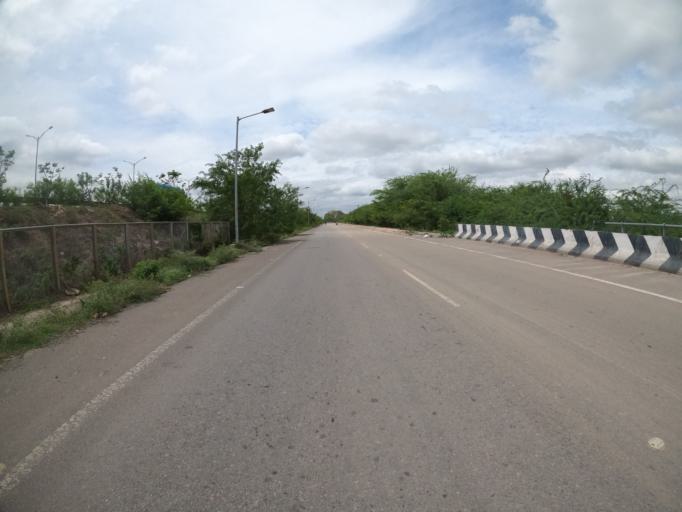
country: IN
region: Telangana
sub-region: Hyderabad
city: Hyderabad
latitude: 17.3026
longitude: 78.3784
